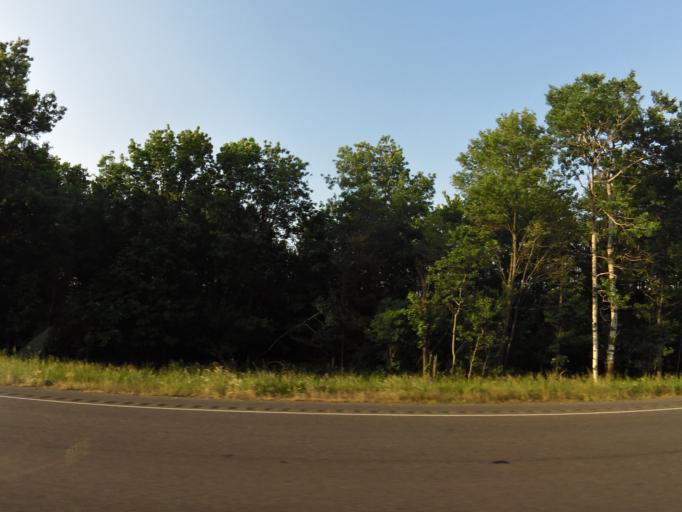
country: US
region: Wisconsin
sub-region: Jackson County
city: Black River Falls
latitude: 44.2485
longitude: -90.7463
